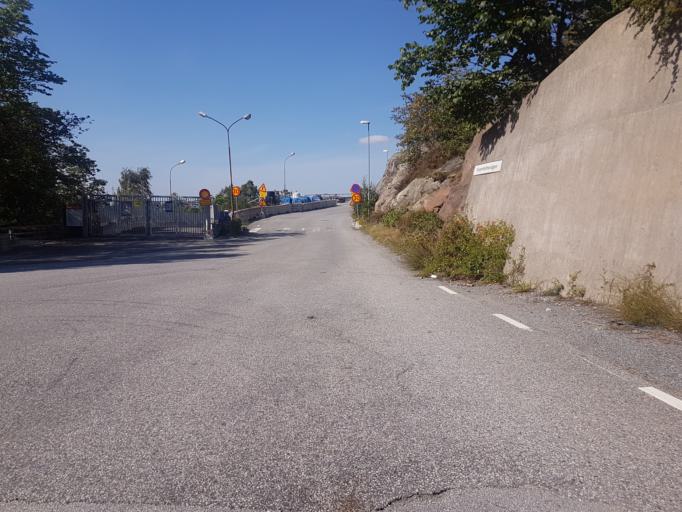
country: SE
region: Stockholm
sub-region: Nacka Kommun
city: Nacka
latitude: 59.3156
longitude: 18.1329
